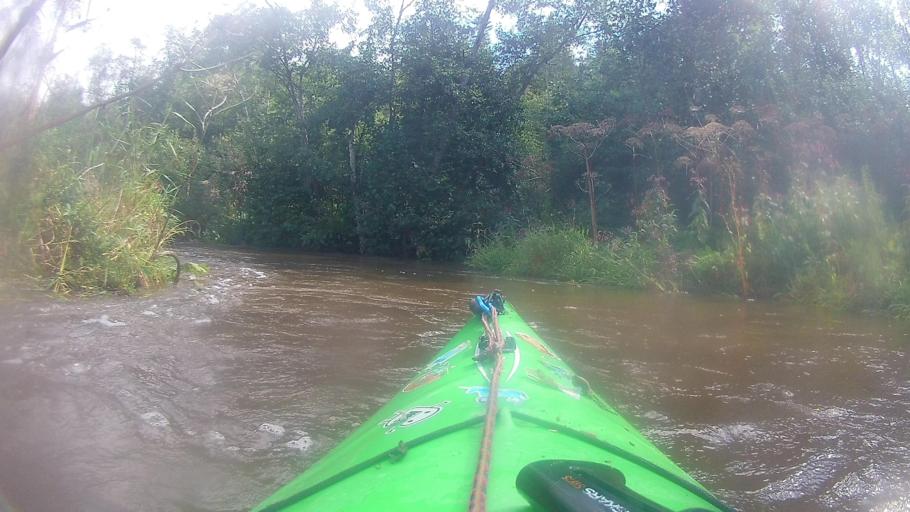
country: LV
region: Talsu Rajons
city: Sabile
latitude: 56.9997
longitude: 22.6056
